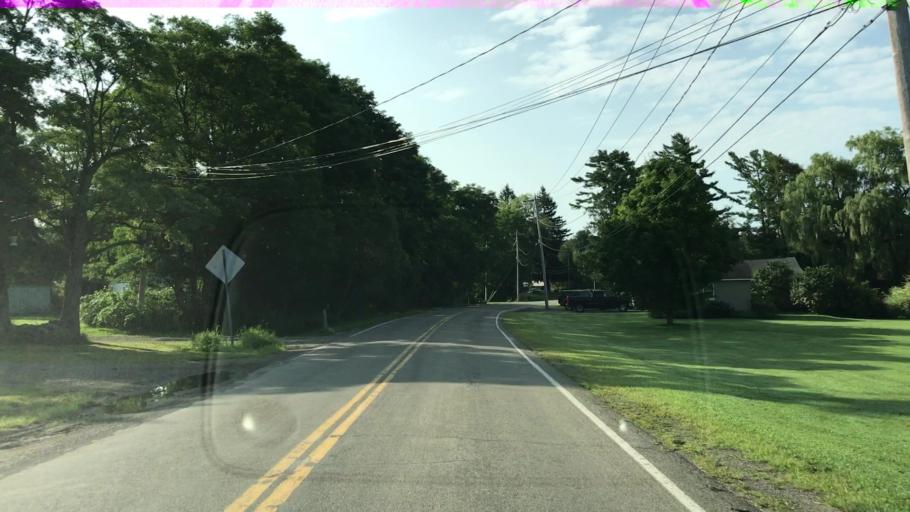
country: US
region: New York
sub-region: Chautauqua County
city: Mayville
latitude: 42.2665
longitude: -79.4718
